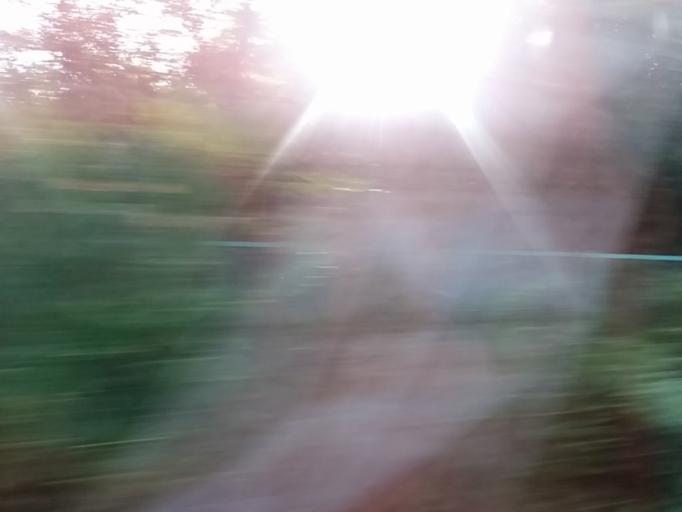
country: JP
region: Nara
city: Nara-shi
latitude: 34.7112
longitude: 135.7921
